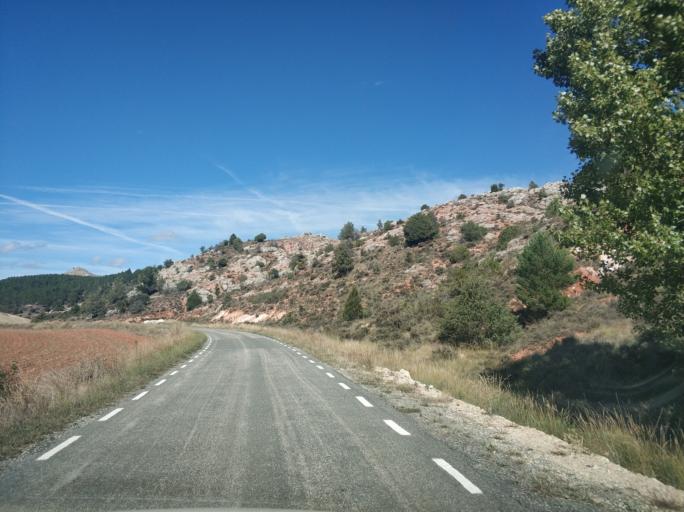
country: ES
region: Castille and Leon
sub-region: Provincia de Soria
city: Espeja de San Marcelino
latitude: 41.8117
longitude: -3.2243
